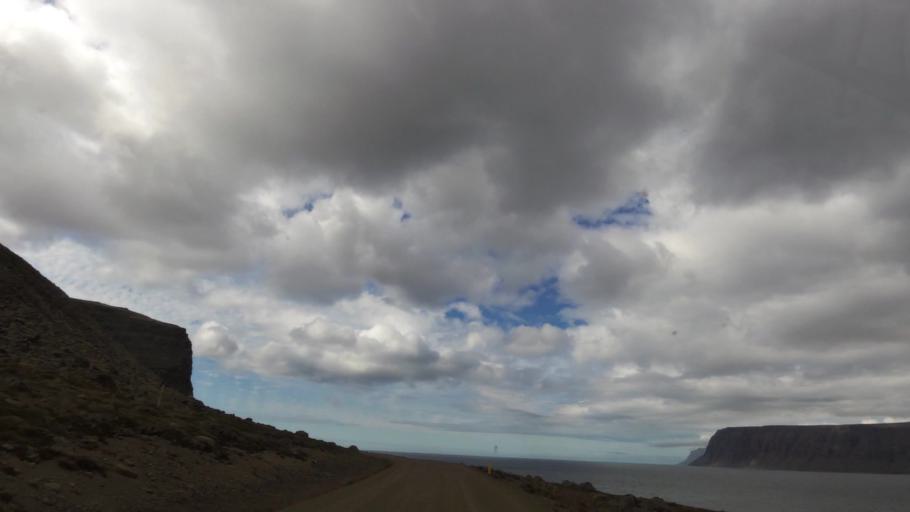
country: IS
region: West
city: Olafsvik
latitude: 65.5750
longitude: -24.0660
